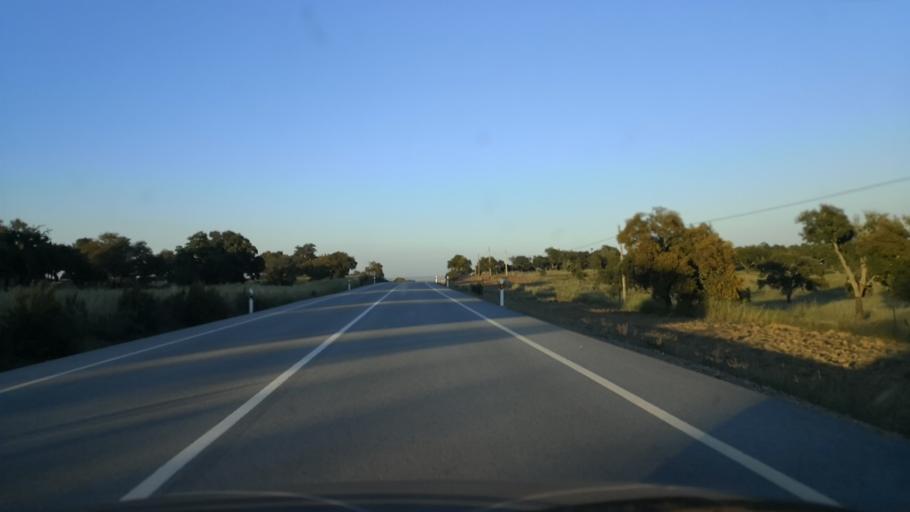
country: ES
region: Extremadura
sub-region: Provincia de Caceres
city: Salorino
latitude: 39.5084
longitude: -7.1180
